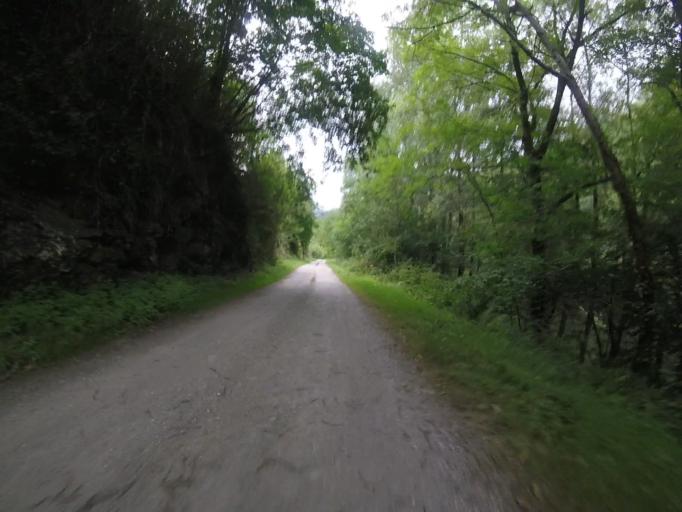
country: ES
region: Navarre
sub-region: Provincia de Navarra
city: Sunbilla
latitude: 43.1934
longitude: -1.6656
